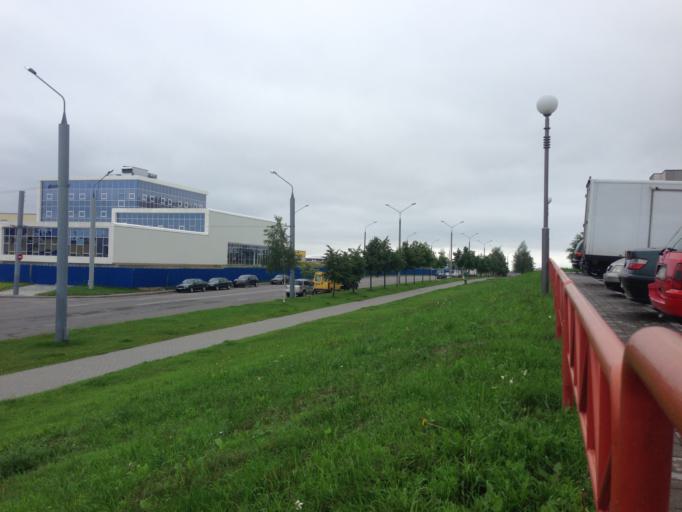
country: BY
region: Grodnenskaya
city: Hrodna
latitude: 53.7126
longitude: 23.8403
